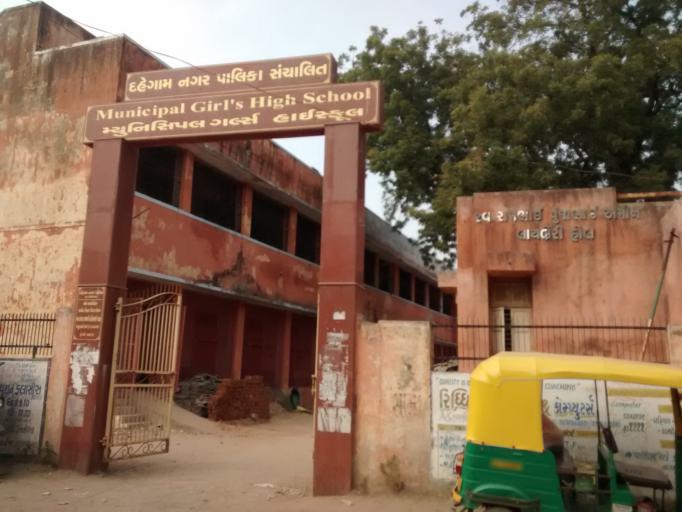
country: IN
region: Gujarat
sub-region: Gandhinagar
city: Dahegam
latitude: 23.1696
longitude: 72.8221
